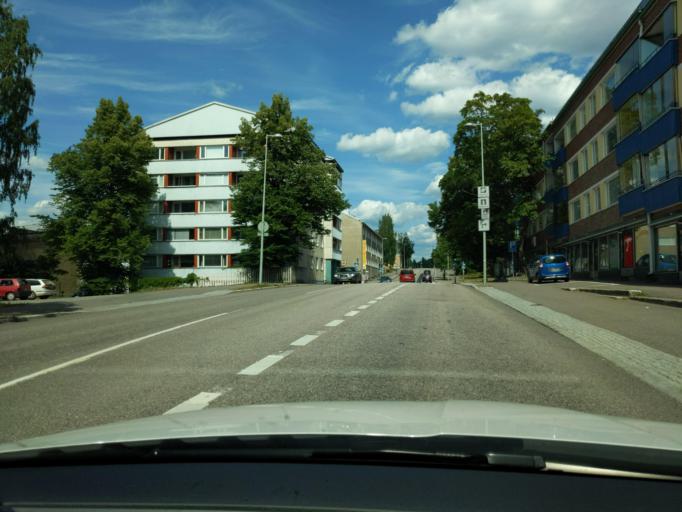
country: FI
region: Paijanne Tavastia
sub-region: Lahti
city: Heinola
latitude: 61.2005
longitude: 26.0350
